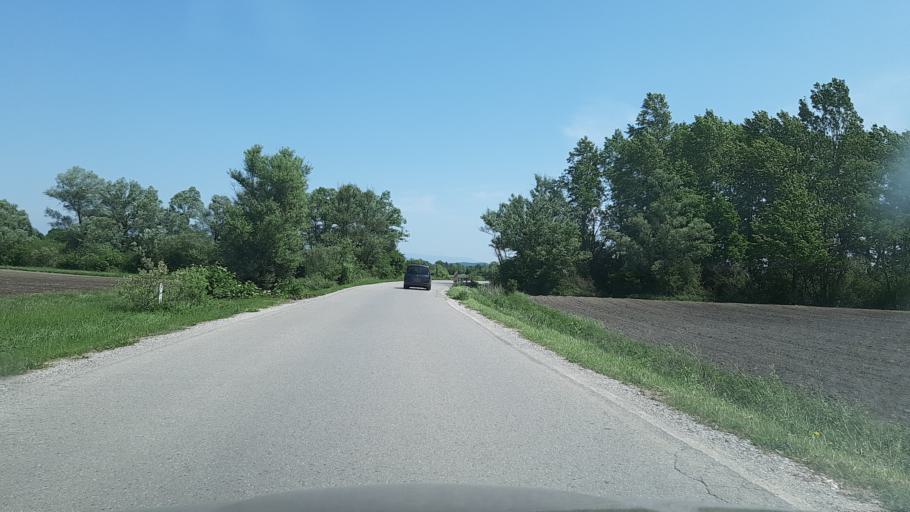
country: SI
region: Brezovica
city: Vnanje Gorice
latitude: 45.9850
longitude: 14.4373
